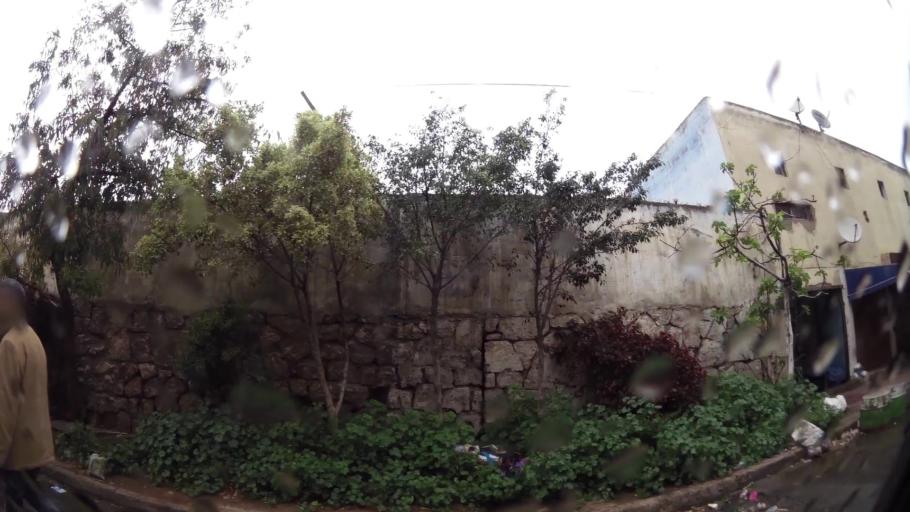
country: MA
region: Grand Casablanca
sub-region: Mediouna
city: Tit Mellil
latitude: 33.6185
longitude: -7.4915
